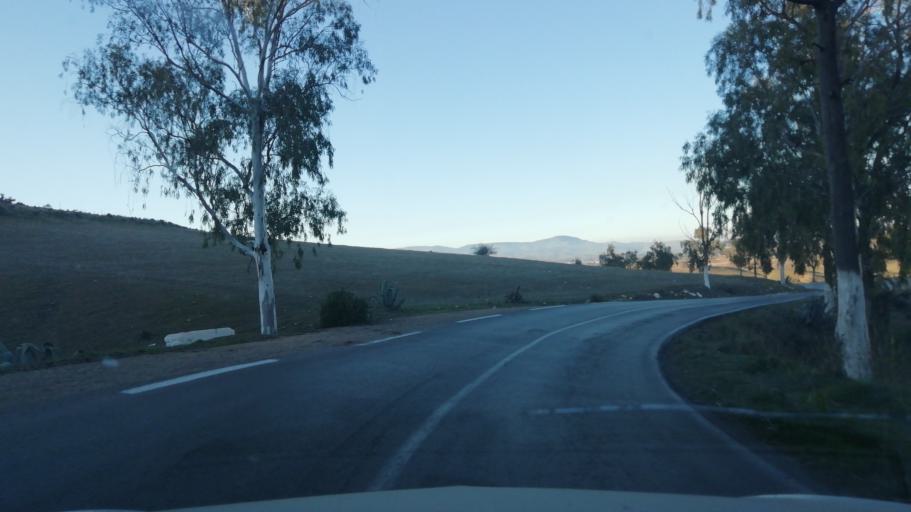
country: DZ
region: Tlemcen
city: Nedroma
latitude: 34.8258
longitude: -1.6392
